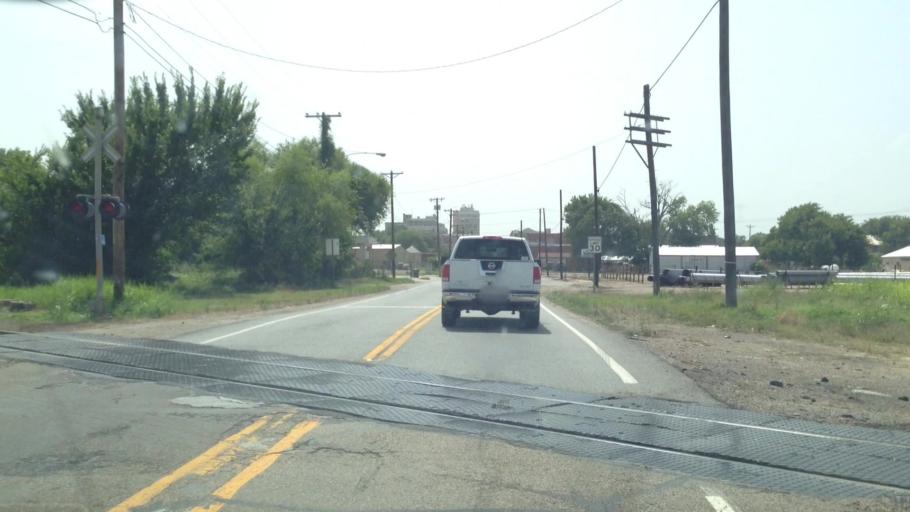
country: US
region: Texas
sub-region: Hunt County
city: Greenville
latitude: 33.1398
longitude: -96.1006
